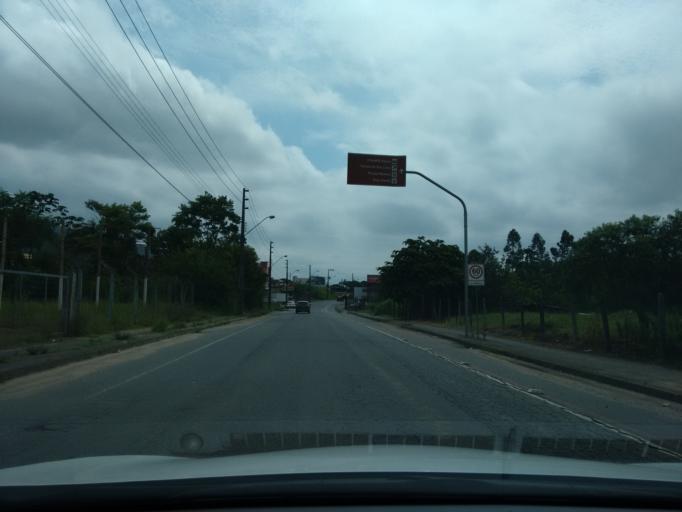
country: BR
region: Santa Catarina
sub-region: Jaragua Do Sul
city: Jaragua do Sul
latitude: -26.4887
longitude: -49.0569
